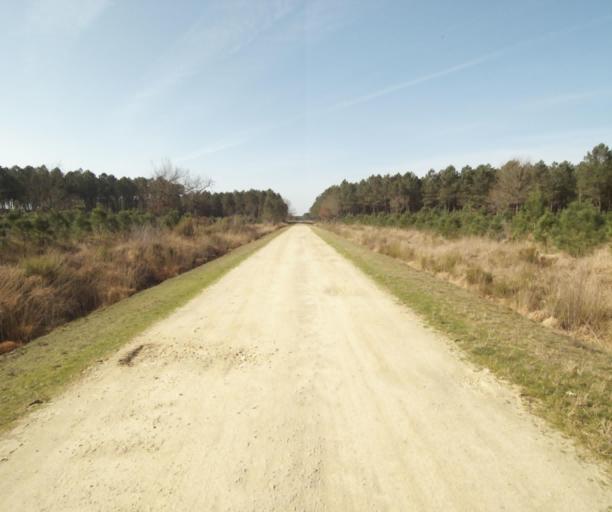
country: FR
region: Aquitaine
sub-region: Departement des Landes
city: Roquefort
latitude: 44.2224
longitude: -0.2443
